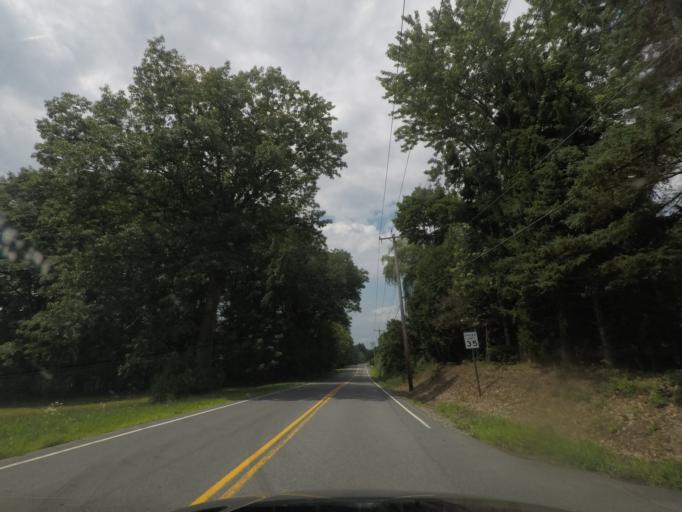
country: US
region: New York
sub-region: Rensselaer County
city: Hampton Manor
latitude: 42.6452
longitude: -73.6841
